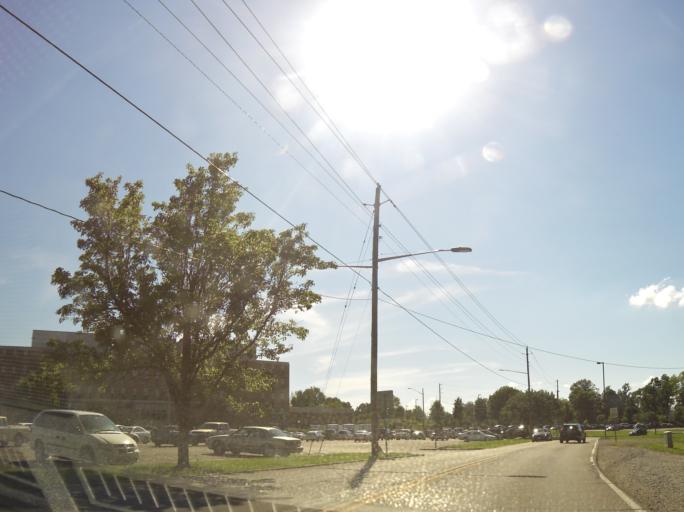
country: US
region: Ohio
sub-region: Greene County
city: Wright-Patterson AFB
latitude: 39.7845
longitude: -84.0611
